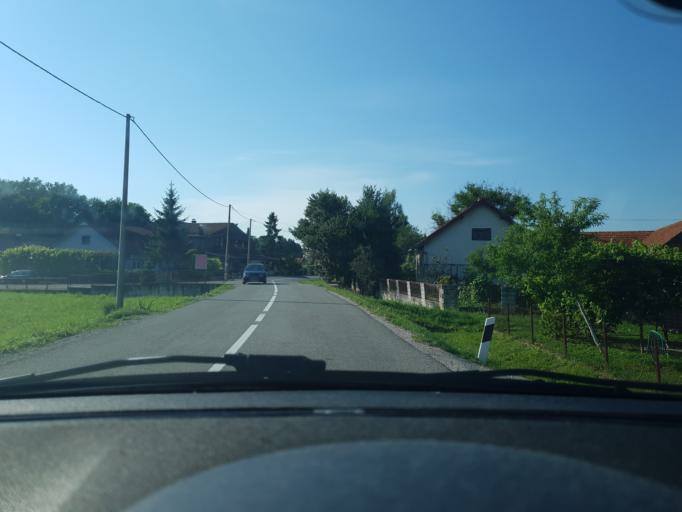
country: HR
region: Zagrebacka
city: Jakovlje
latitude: 45.9226
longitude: 15.8428
